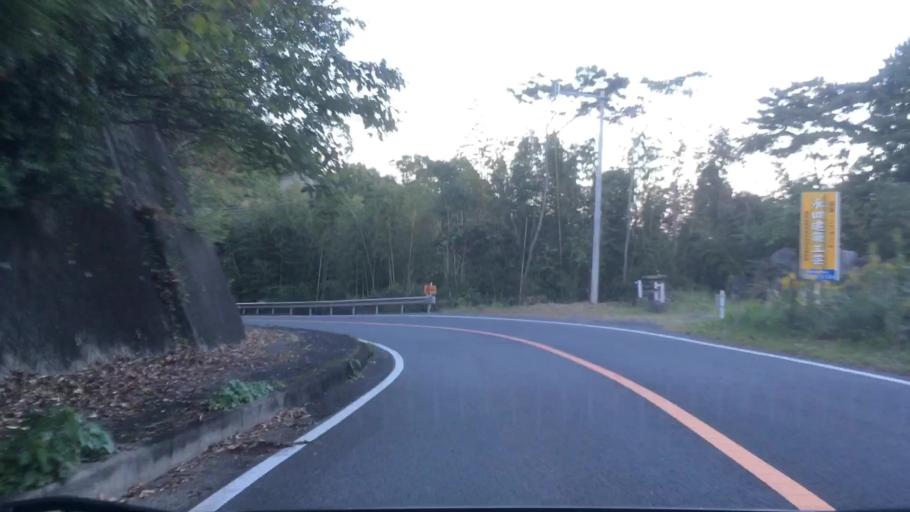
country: JP
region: Nagasaki
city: Sasebo
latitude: 32.9976
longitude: 129.7259
